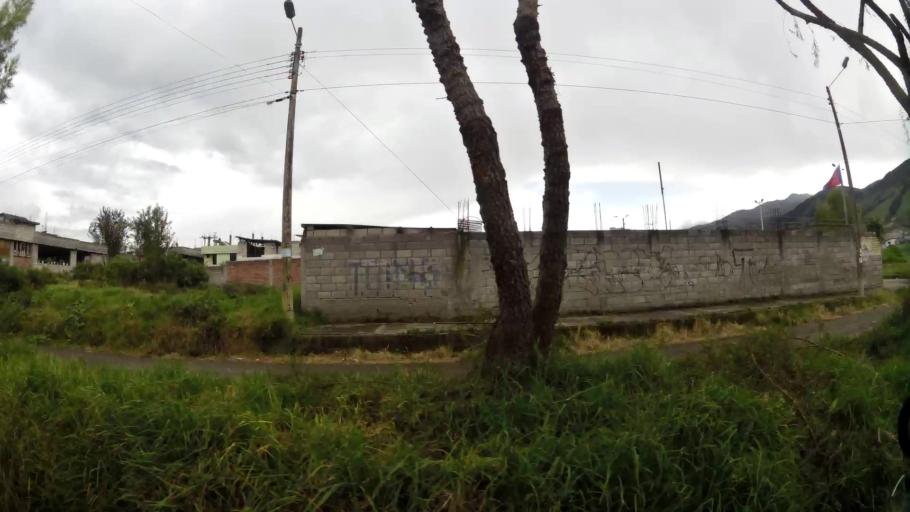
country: EC
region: Pichincha
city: Quito
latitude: -0.3098
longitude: -78.5559
